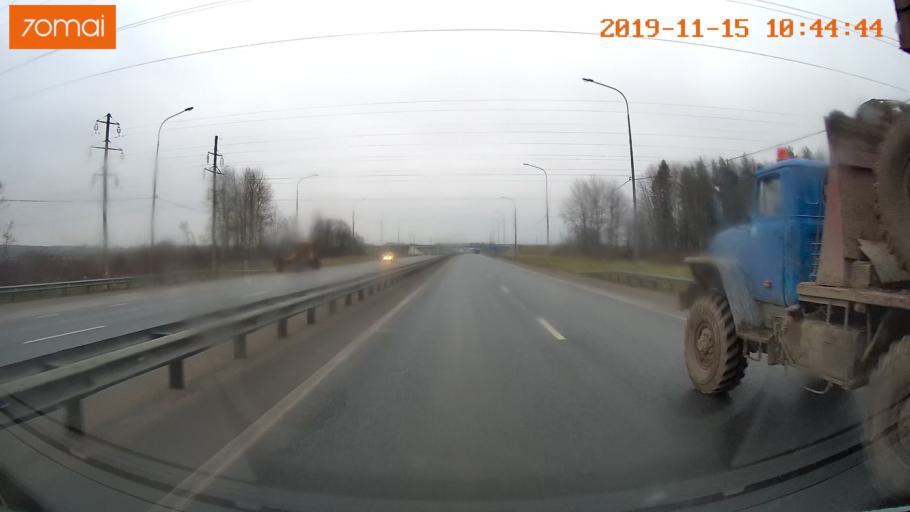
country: RU
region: Vologda
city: Sheksna
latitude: 59.2114
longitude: 38.5664
